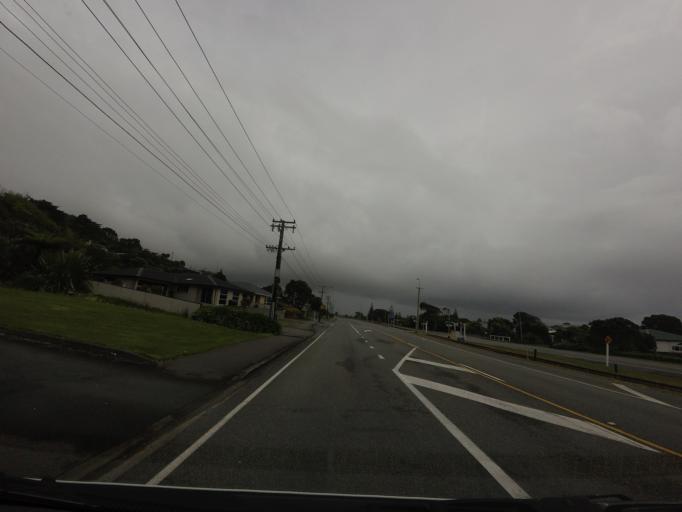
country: NZ
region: West Coast
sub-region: Grey District
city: Greymouth
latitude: -42.4706
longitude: 171.1891
